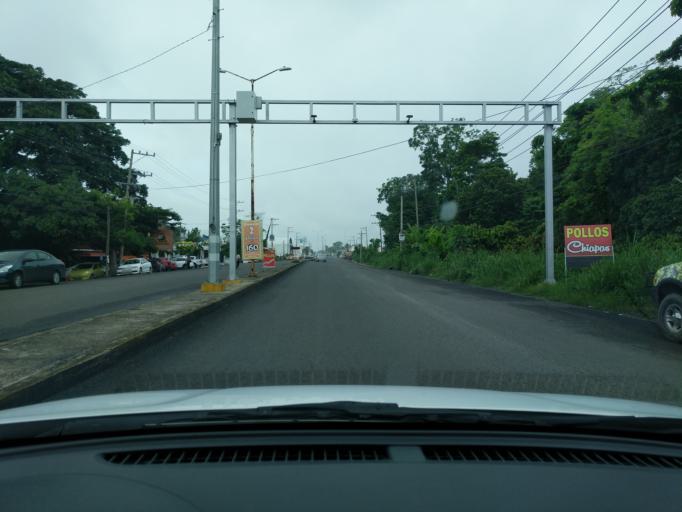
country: MX
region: Tabasco
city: Villahermosa
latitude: 17.9605
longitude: -92.9650
